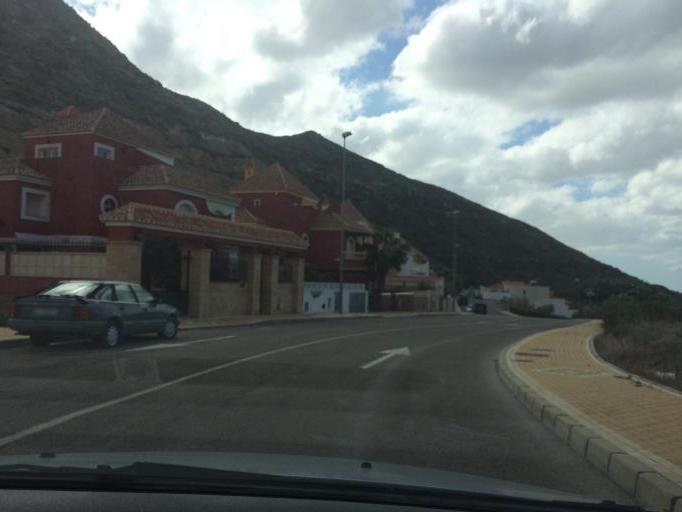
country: ES
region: Andalusia
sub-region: Provincia de Almeria
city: Vicar
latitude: 36.8311
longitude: -2.6120
